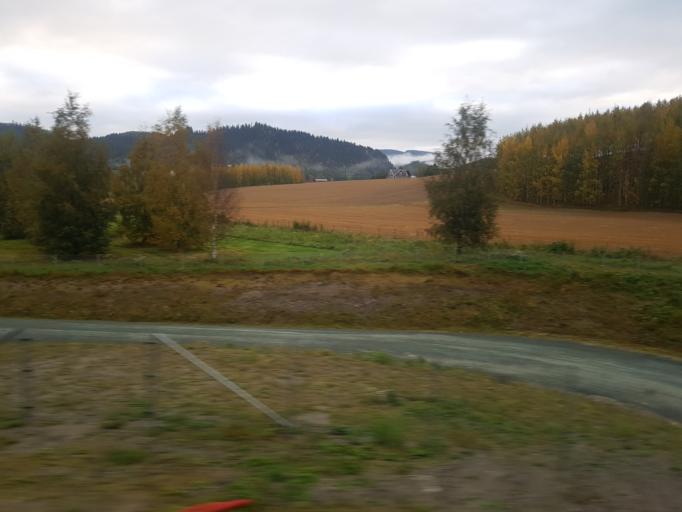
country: NO
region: Sor-Trondelag
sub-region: Melhus
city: Lundamo
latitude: 63.1962
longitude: 10.3043
